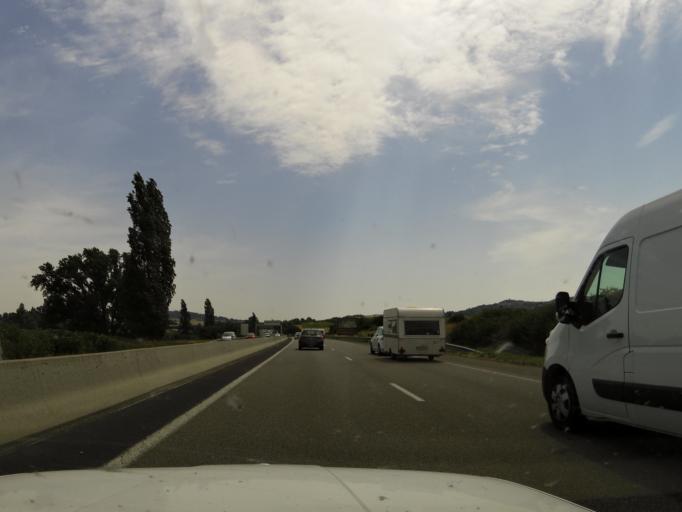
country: FR
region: Auvergne
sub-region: Departement du Puy-de-Dome
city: Orcet
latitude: 45.7129
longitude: 3.1512
